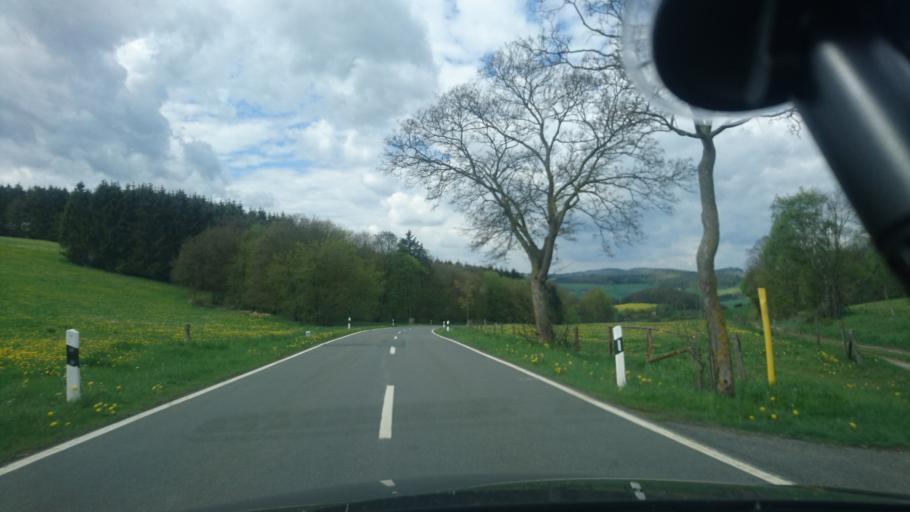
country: DE
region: North Rhine-Westphalia
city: Marsberg
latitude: 51.3579
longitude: 8.7469
